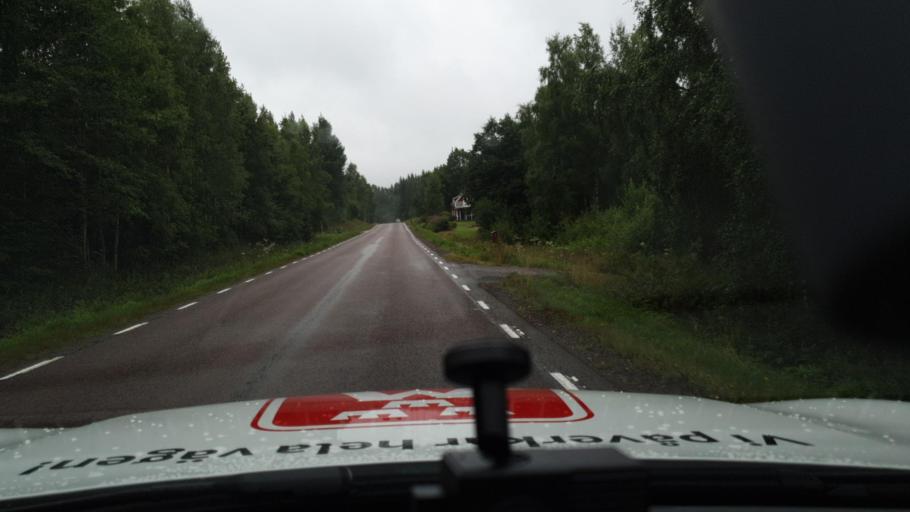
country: SE
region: Vaermland
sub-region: Torsby Kommun
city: Torsby
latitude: 59.9408
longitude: 12.7455
